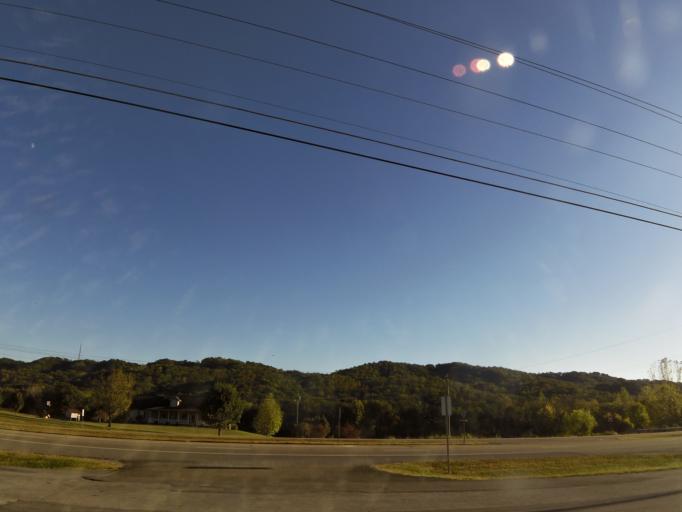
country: US
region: Tennessee
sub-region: Grainger County
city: Bean Station
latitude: 36.3473
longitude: -83.3133
